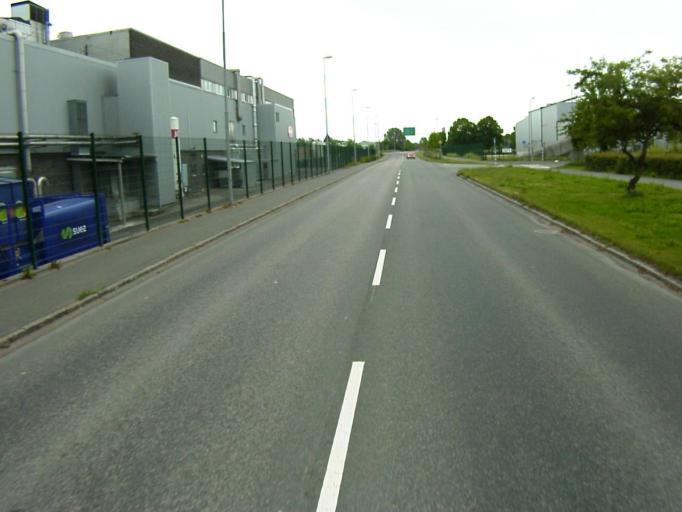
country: SE
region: Skane
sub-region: Kristianstads Kommun
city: Kristianstad
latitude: 56.0196
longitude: 14.1463
